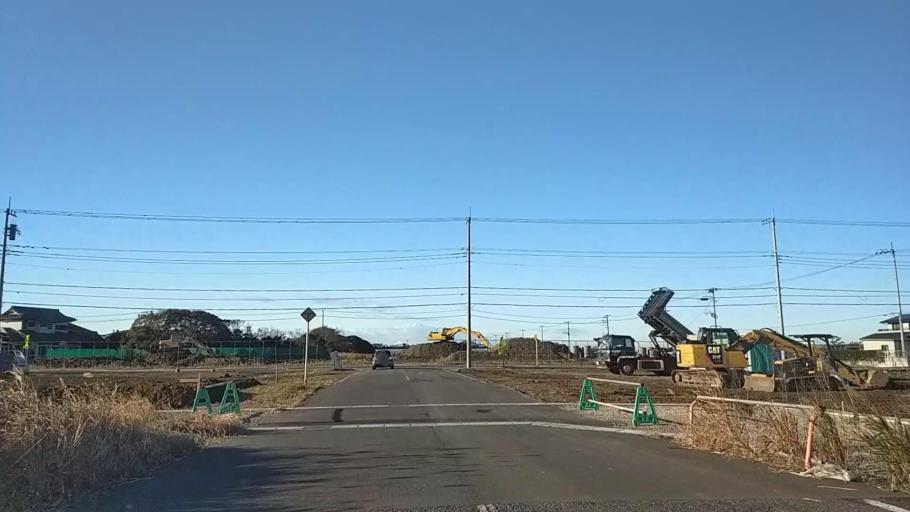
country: JP
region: Chiba
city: Kisarazu
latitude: 35.4246
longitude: 139.9180
